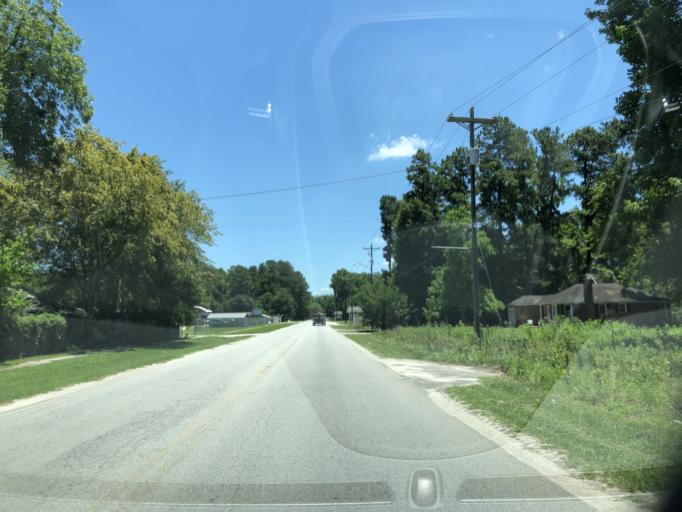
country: US
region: South Carolina
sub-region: Orangeburg County
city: Branchville
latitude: 33.2523
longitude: -80.8134
